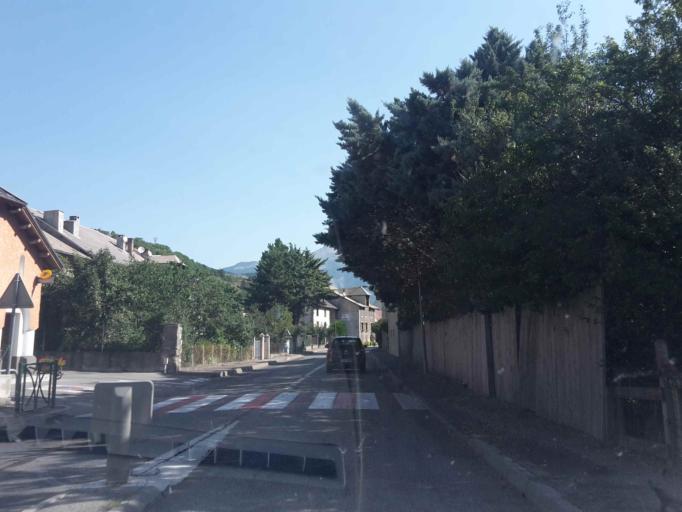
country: FR
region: Provence-Alpes-Cote d'Azur
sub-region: Departement des Hautes-Alpes
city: Guillestre
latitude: 44.6478
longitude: 6.5777
